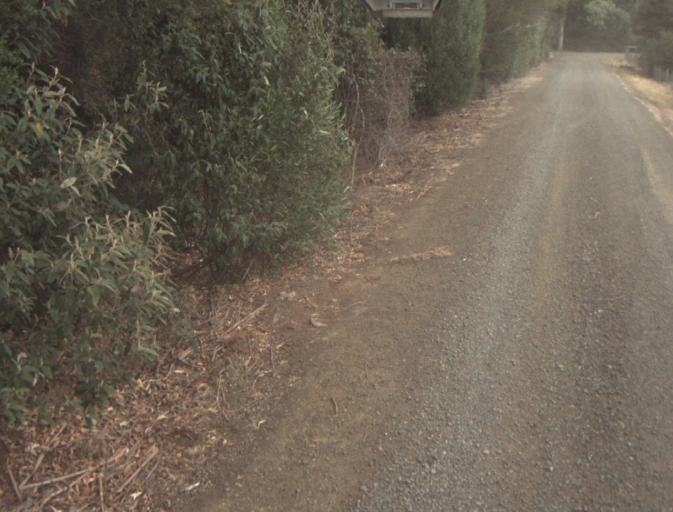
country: AU
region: Tasmania
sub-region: Launceston
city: Mayfield
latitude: -41.2714
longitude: 147.1851
